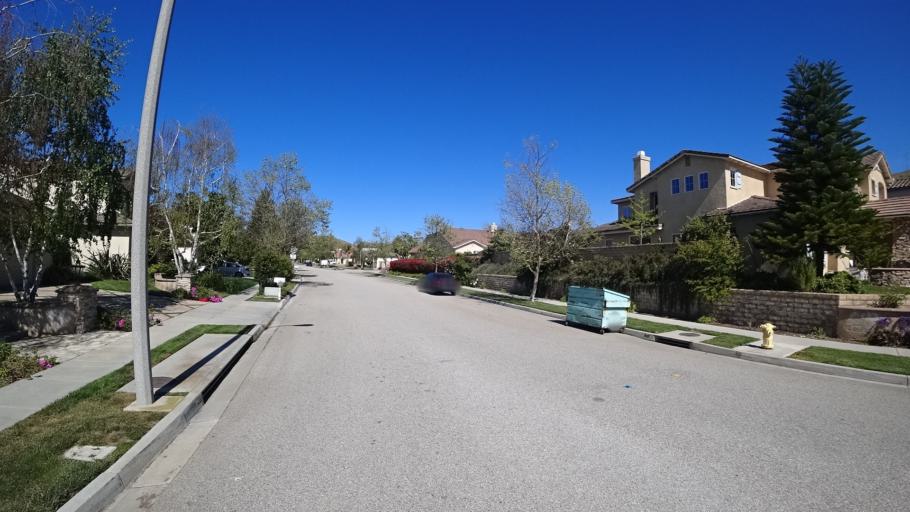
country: US
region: California
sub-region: Ventura County
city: Casa Conejo
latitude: 34.1763
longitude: -118.9845
